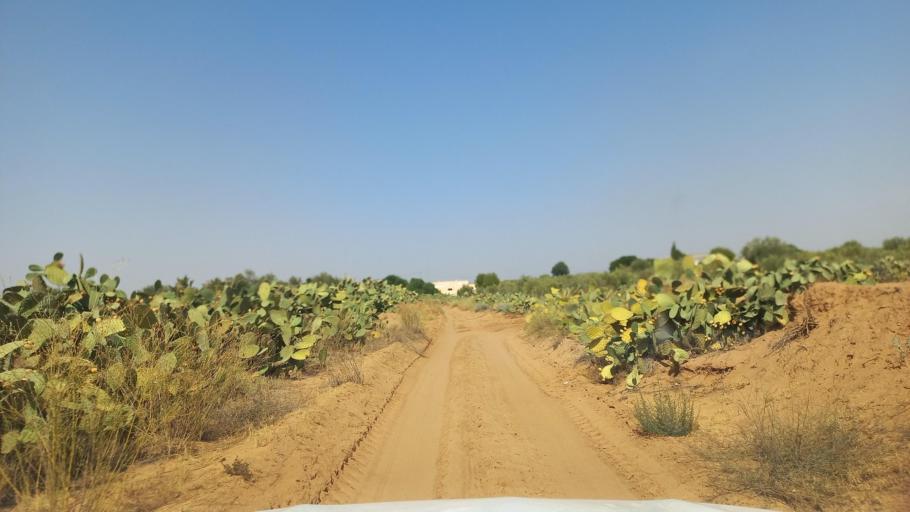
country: TN
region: Al Qasrayn
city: Kasserine
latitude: 35.2412
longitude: 9.0594
